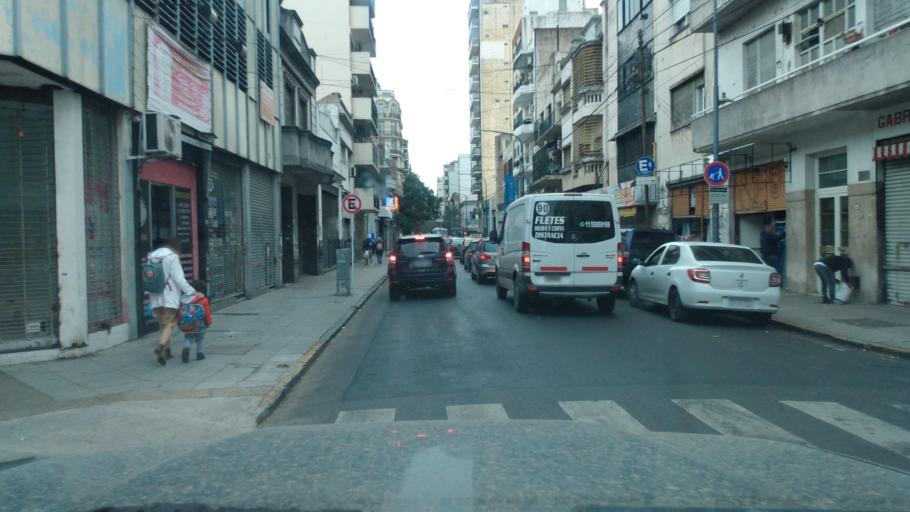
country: AR
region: Buenos Aires F.D.
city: Buenos Aires
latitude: -34.6033
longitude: -58.3970
